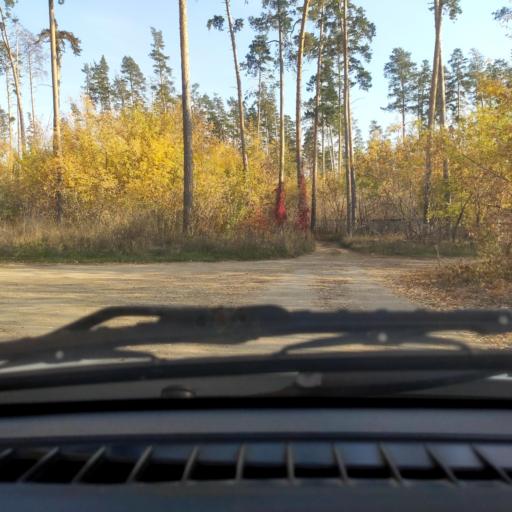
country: RU
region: Samara
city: Tol'yatti
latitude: 53.4787
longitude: 49.3703
